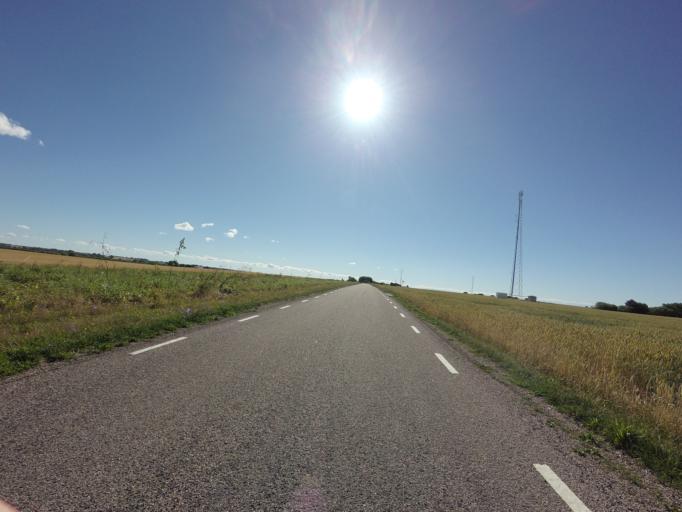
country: SE
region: Skane
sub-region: Trelleborgs Kommun
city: Skare
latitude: 55.3909
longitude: 13.0613
